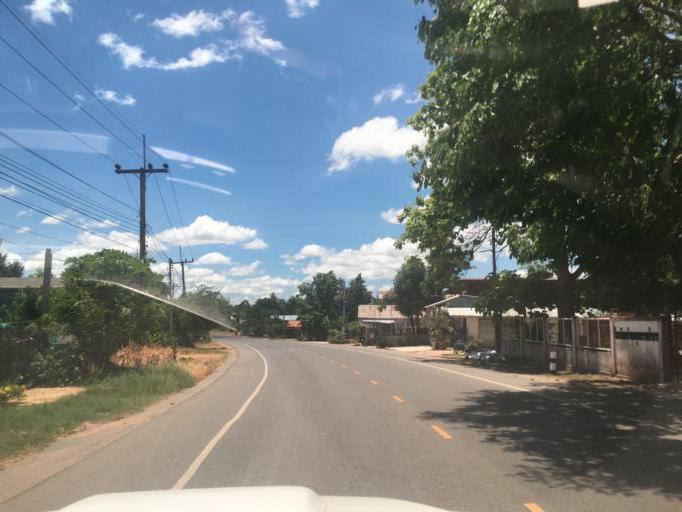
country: TH
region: Changwat Udon Thani
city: Nong Saeng
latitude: 17.2260
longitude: 102.7426
